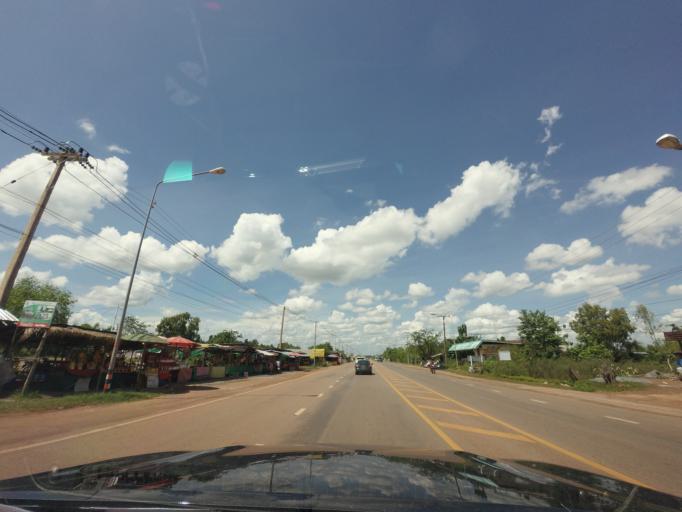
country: TH
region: Changwat Udon Thani
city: Ban Dung
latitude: 17.7111
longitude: 103.2502
